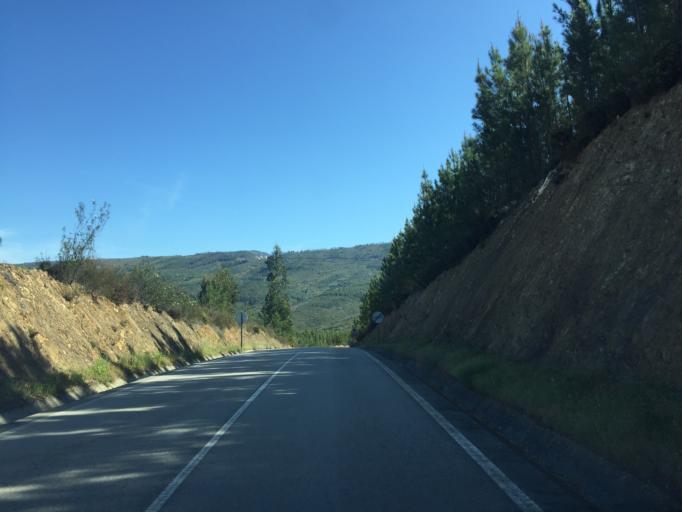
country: PT
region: Coimbra
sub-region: Pampilhosa da Serra
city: Pampilhosa da Serra
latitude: 40.0822
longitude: -7.7955
